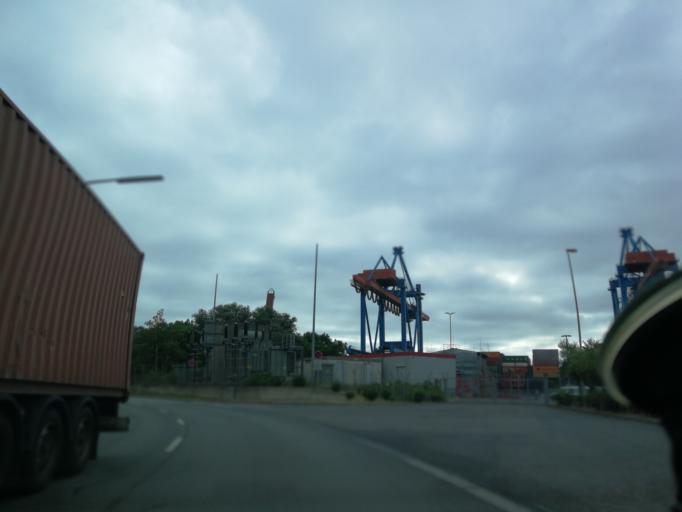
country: DE
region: Hamburg
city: Altona
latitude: 53.5095
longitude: 9.9325
